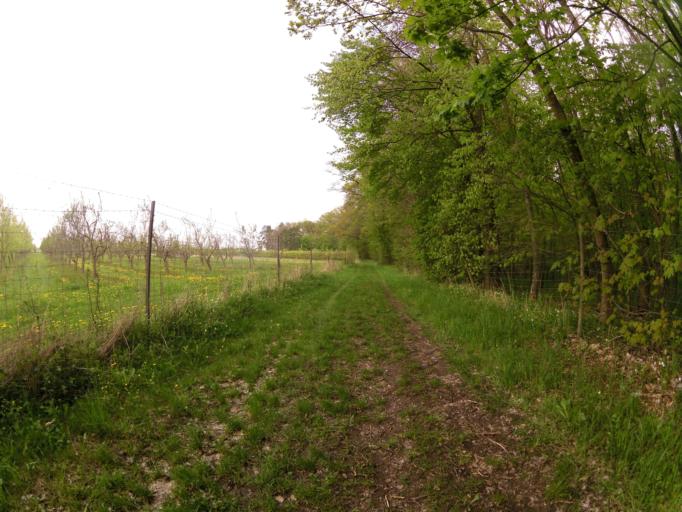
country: DE
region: Bavaria
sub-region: Regierungsbezirk Unterfranken
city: Sommerhausen
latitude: 49.7073
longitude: 10.0548
